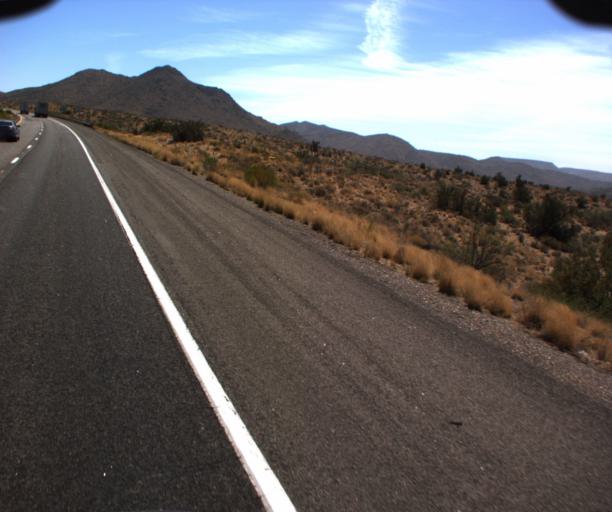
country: US
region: Arizona
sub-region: Mohave County
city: Peach Springs
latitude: 35.1585
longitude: -113.5597
